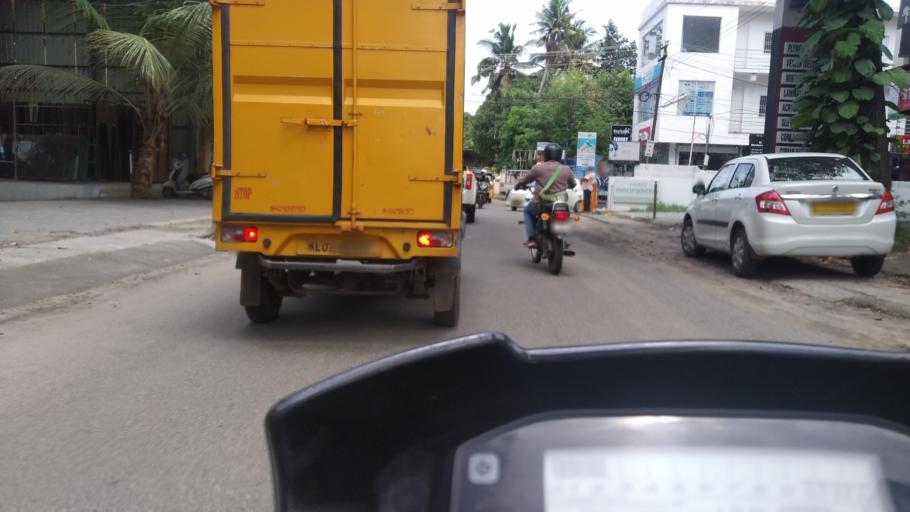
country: IN
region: Kerala
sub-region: Ernakulam
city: Cochin
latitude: 9.9893
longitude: 76.3100
